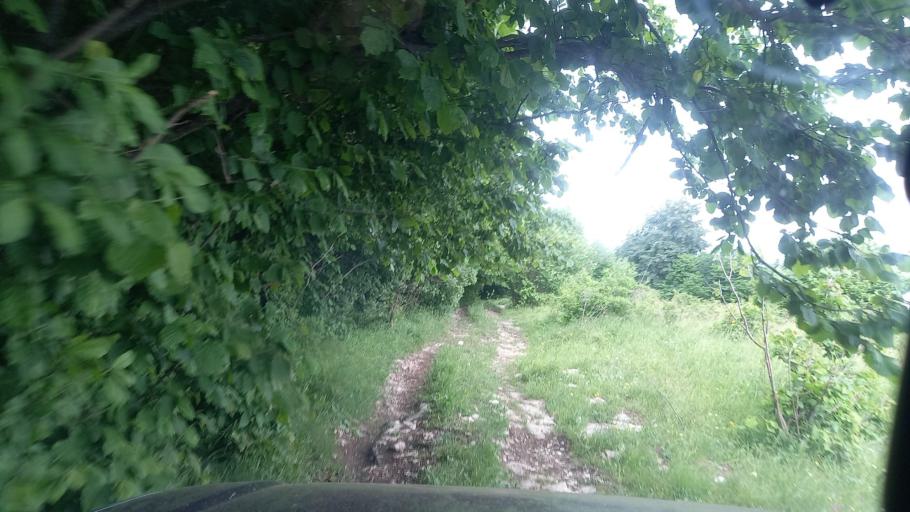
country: RU
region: Karachayevo-Cherkesiya
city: Pregradnaya
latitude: 44.0070
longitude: 41.2787
